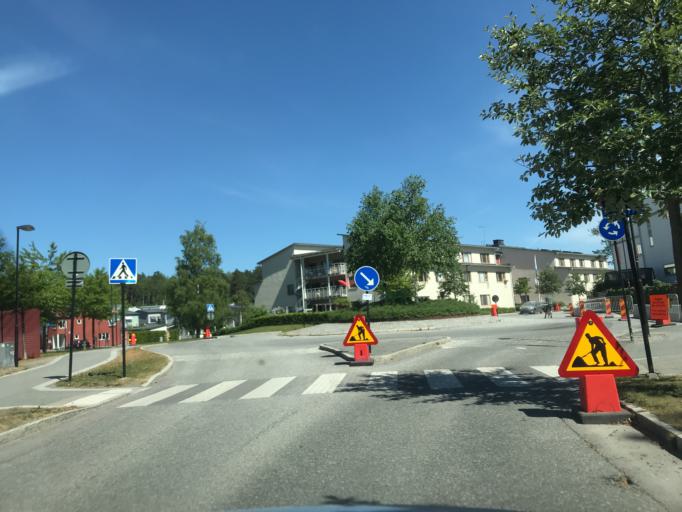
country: SE
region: Stockholm
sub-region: Solna Kommun
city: Rasunda
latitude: 59.4001
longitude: 17.9872
